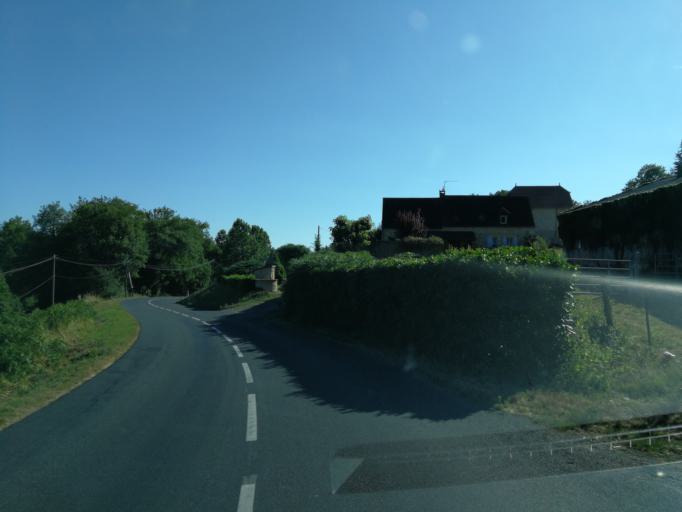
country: FR
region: Midi-Pyrenees
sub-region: Departement du Lot
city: Gourdon
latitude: 44.7156
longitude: 1.3539
